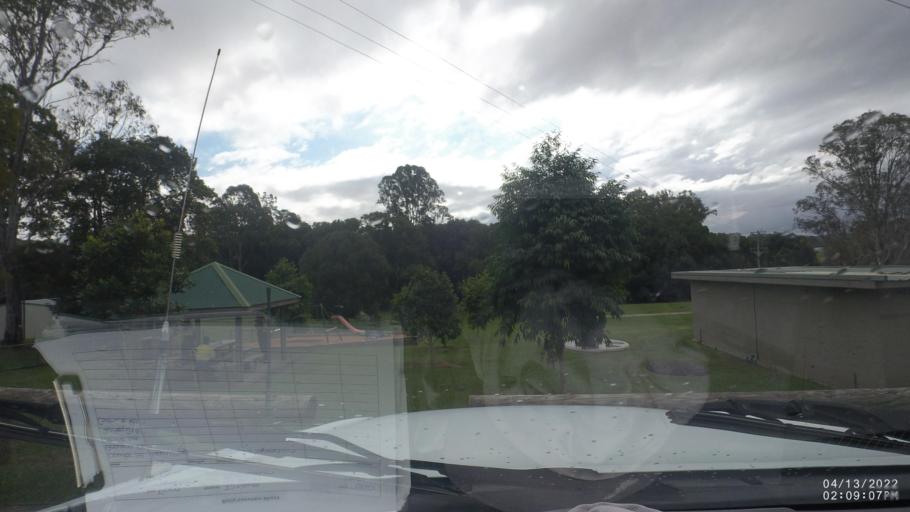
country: AU
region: Queensland
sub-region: Gold Coast
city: Ormeau Hills
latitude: -27.8273
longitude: 153.1791
